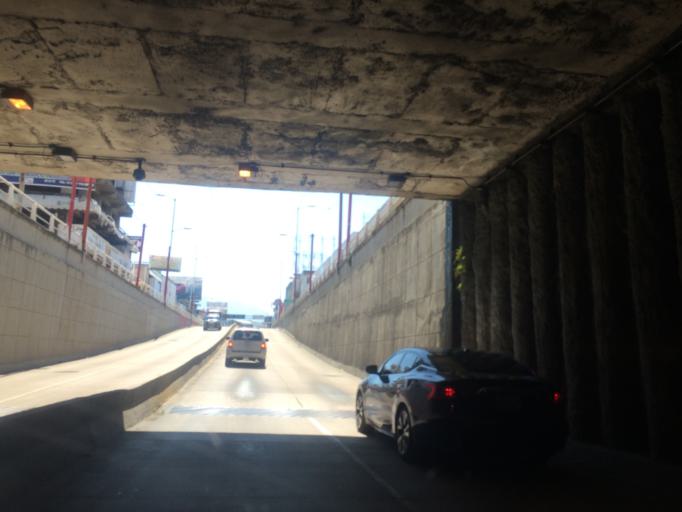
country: MX
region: Nayarit
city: Tepic
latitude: 21.5045
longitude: -104.8954
